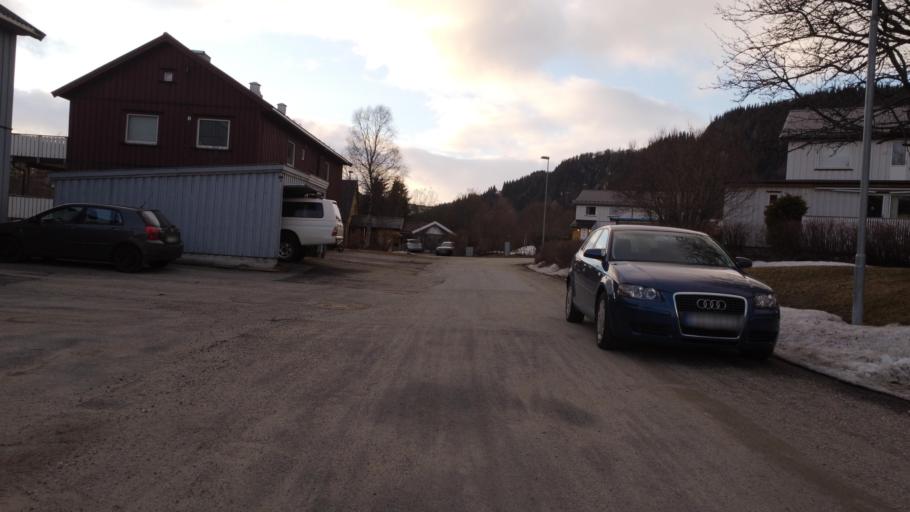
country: NO
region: Nordland
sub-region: Rana
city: Mo i Rana
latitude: 66.3264
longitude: 14.1710
